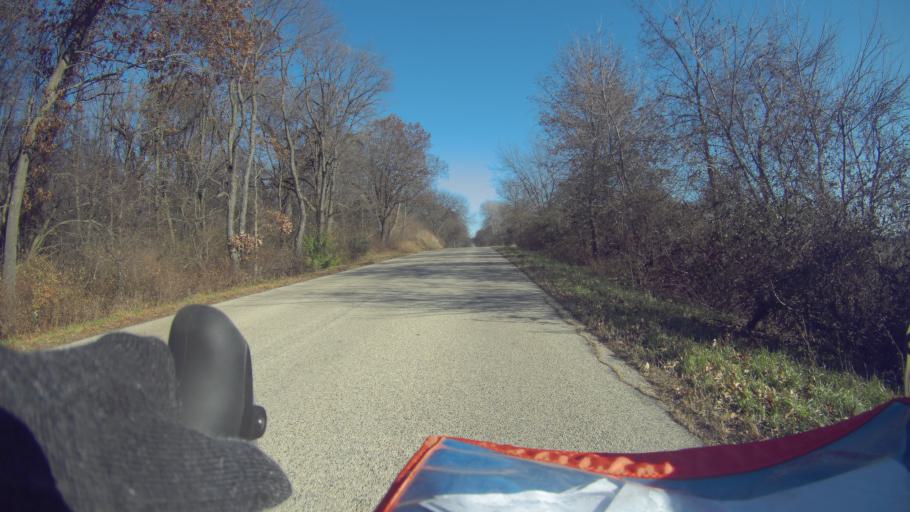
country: US
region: Wisconsin
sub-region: Dane County
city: Stoughton
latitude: 42.8462
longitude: -89.2197
